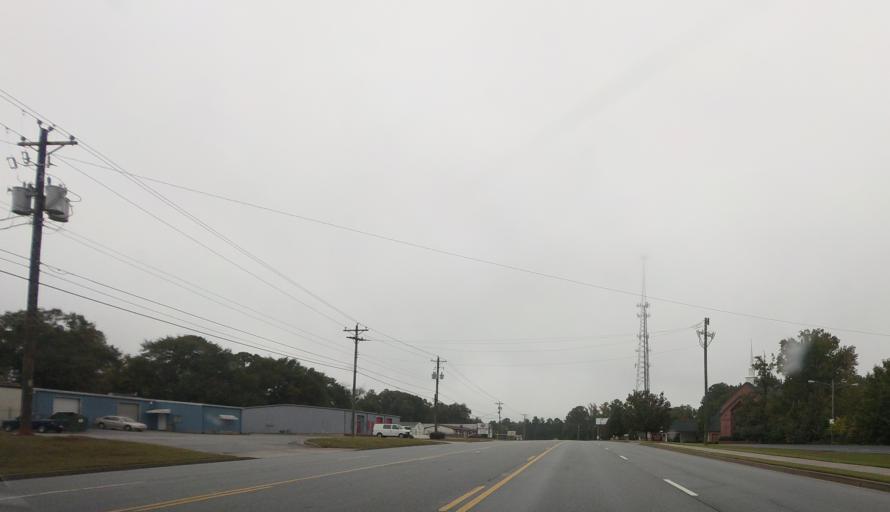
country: US
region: Georgia
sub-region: Houston County
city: Centerville
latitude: 32.6051
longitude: -83.6650
